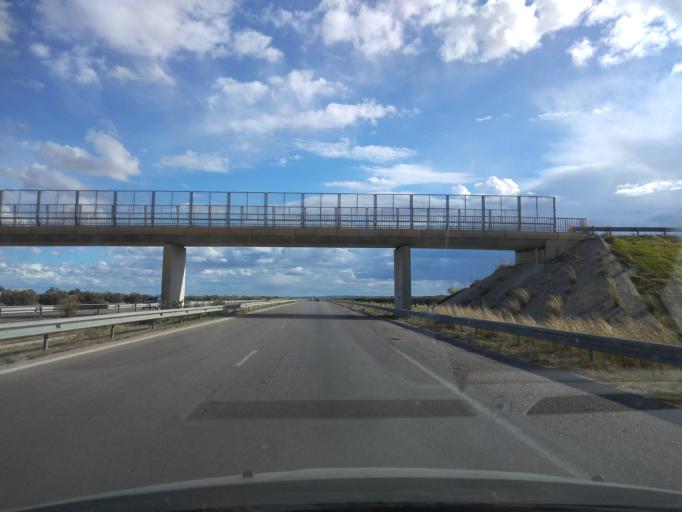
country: TN
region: Al Munastir
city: Manzil Kamil
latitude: 35.6187
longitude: 10.5949
